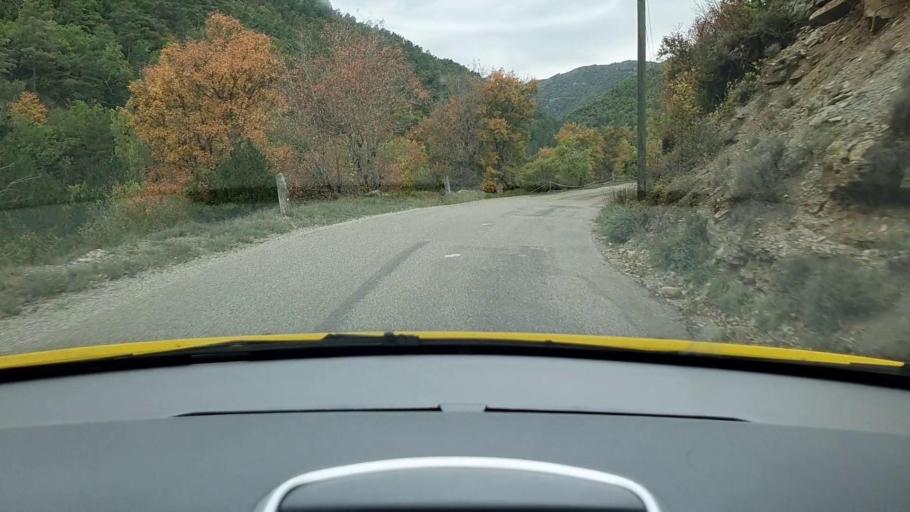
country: FR
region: Languedoc-Roussillon
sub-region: Departement de la Lozere
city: Meyrueis
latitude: 44.0756
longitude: 3.3642
